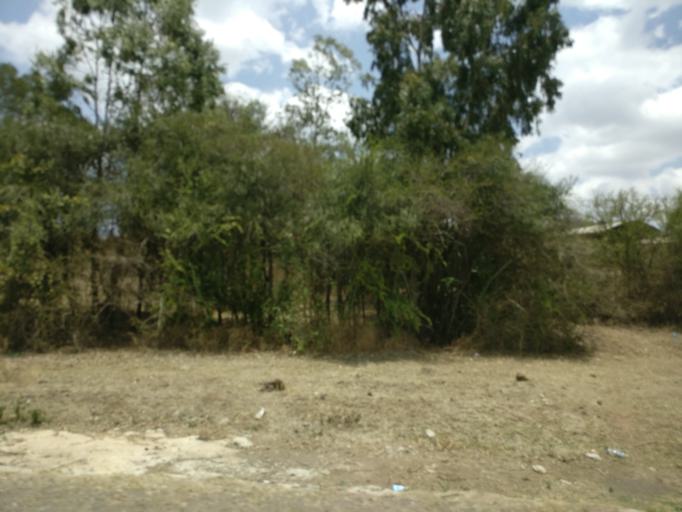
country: ET
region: Oromiya
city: Bishoftu
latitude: 8.7849
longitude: 38.9872
